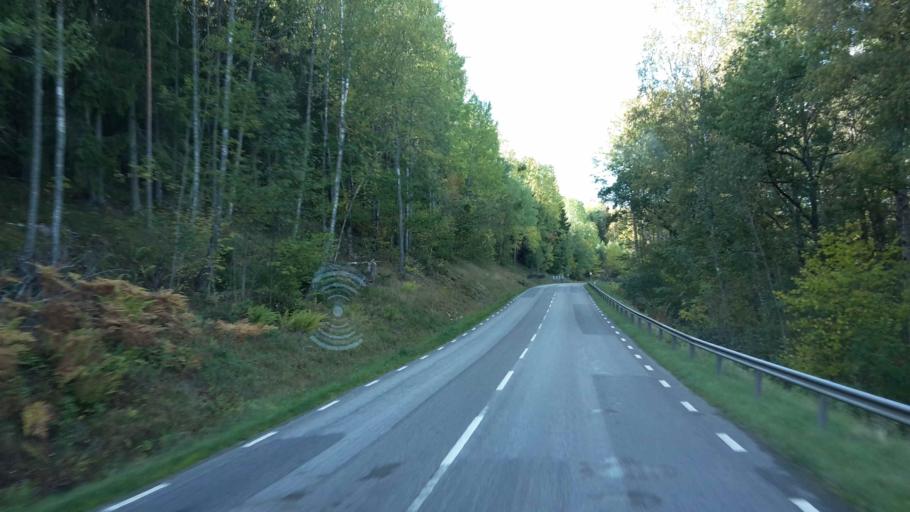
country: SE
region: OEstergoetland
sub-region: Atvidabergs Kommun
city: Atvidaberg
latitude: 58.1785
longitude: 16.1141
